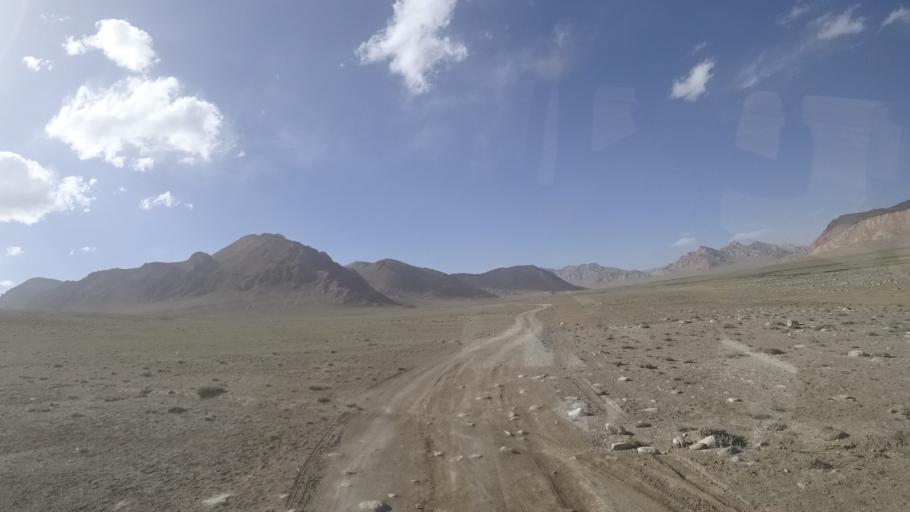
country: TJ
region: Gorno-Badakhshan
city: Murghob
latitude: 37.5860
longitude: 74.1534
